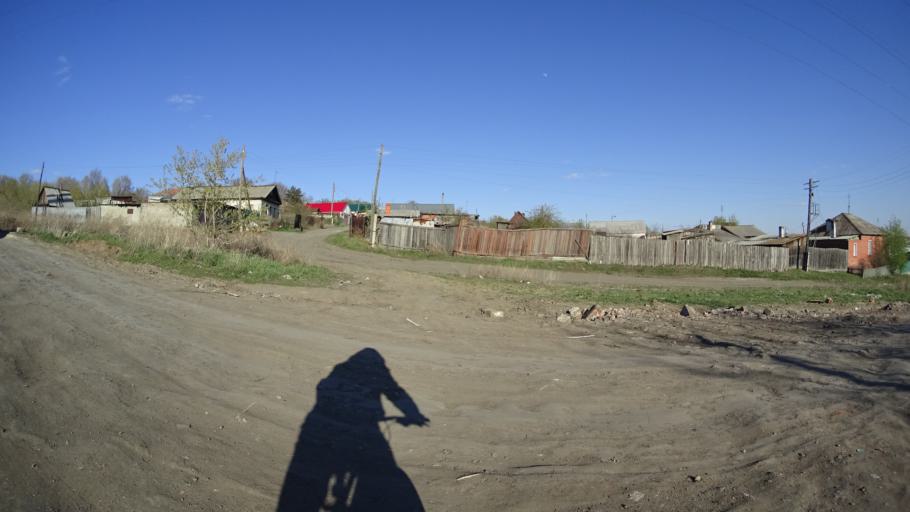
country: RU
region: Chelyabinsk
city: Troitsk
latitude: 54.0984
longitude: 61.5500
